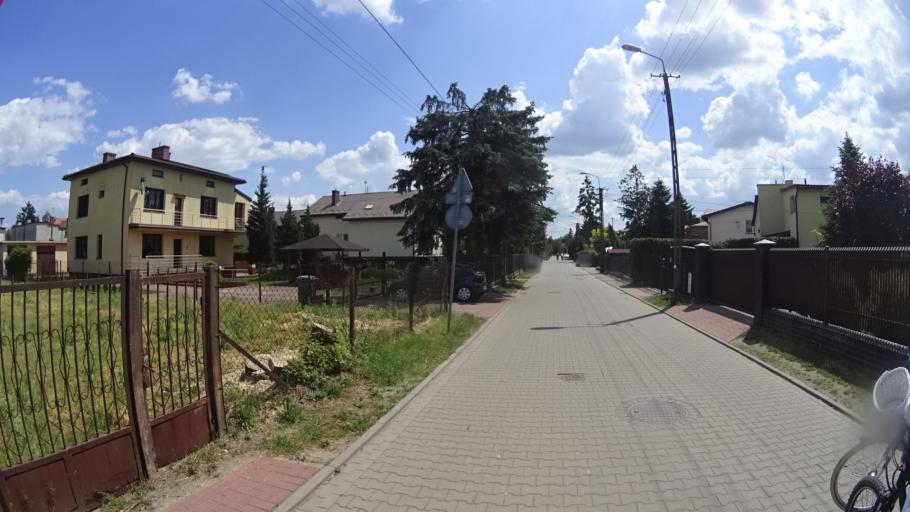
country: PL
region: Masovian Voivodeship
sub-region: Powiat pruszkowski
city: Granica
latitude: 52.1433
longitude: 20.7963
